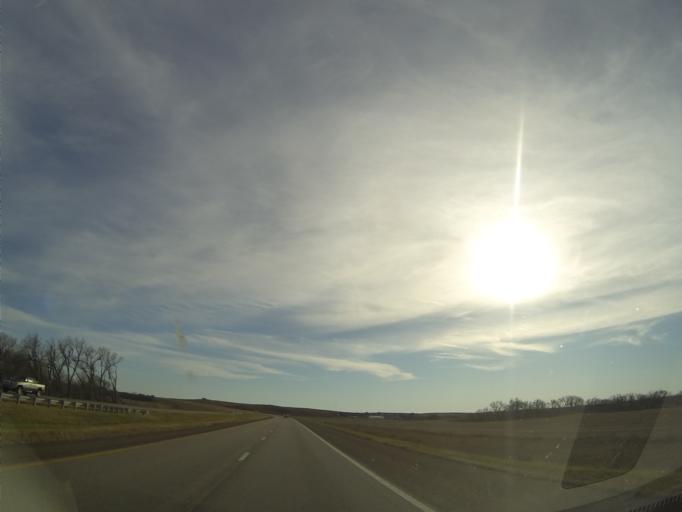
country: US
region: Kansas
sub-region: Ottawa County
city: Minneapolis
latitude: 39.0487
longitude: -97.6517
